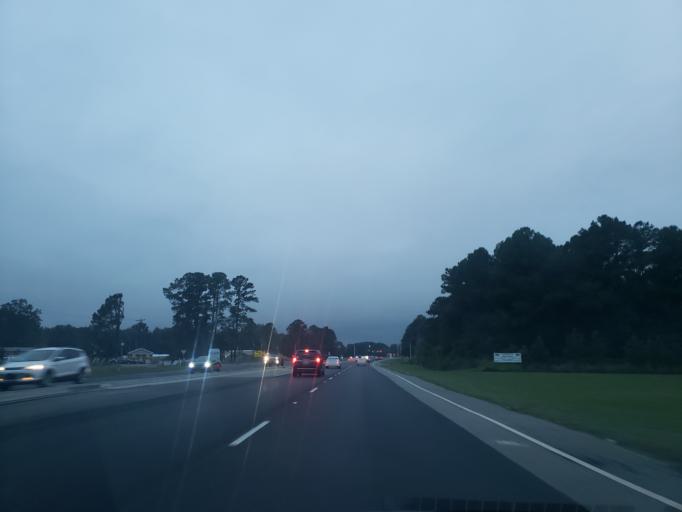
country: US
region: Georgia
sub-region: Chatham County
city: Georgetown
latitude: 31.9968
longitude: -81.2639
